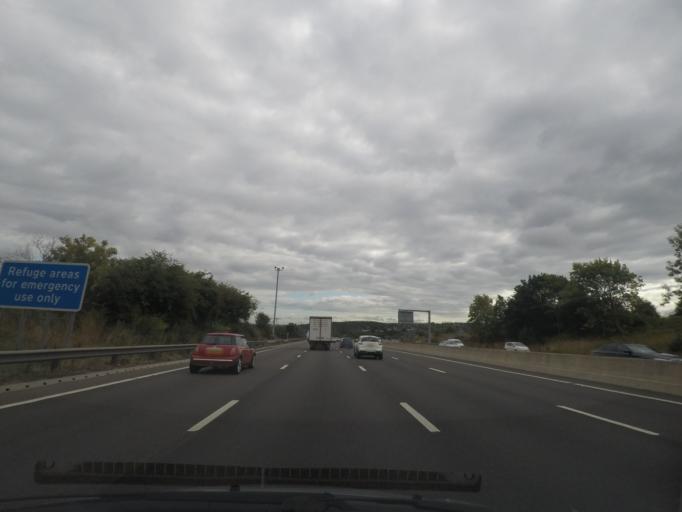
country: GB
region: England
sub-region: Rotherham
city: Wentworth
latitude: 53.4463
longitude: -1.4425
